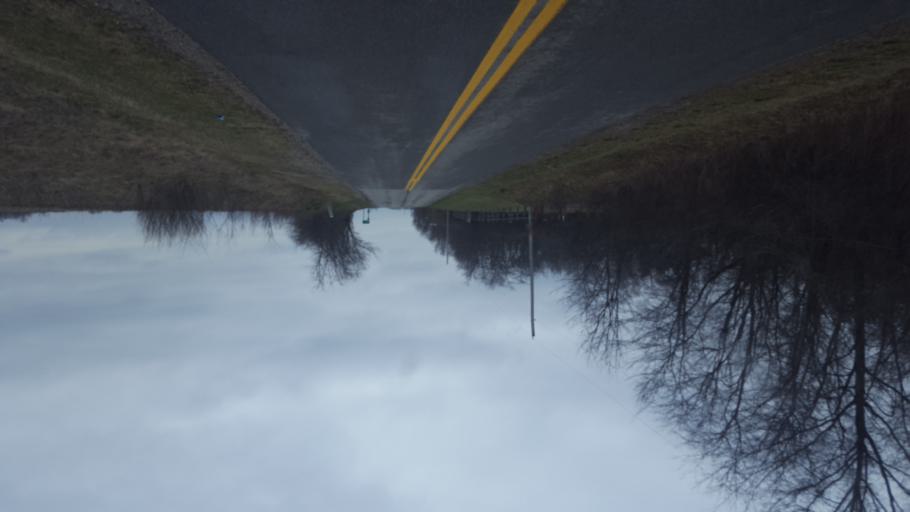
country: US
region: Ohio
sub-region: Delaware County
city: Ashley
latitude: 40.4172
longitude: -83.0099
